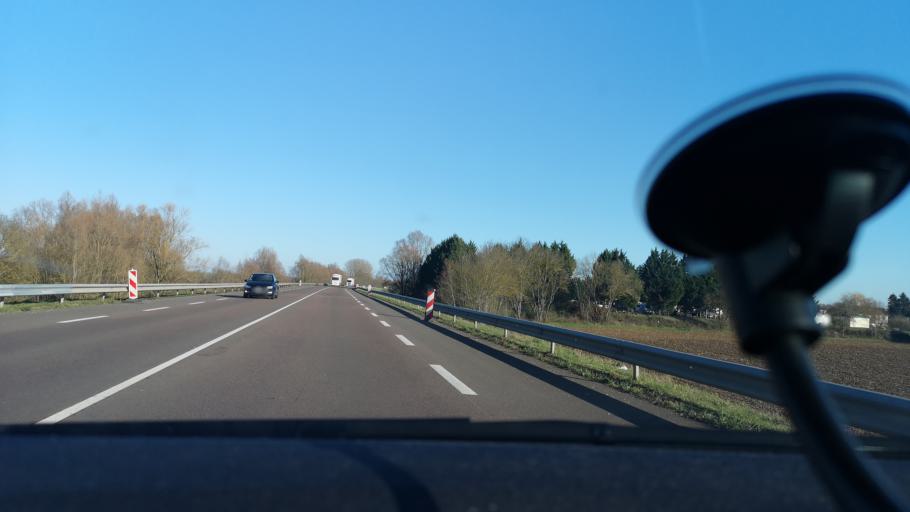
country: FR
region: Bourgogne
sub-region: Departement de Saone-et-Loire
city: Saint-Marcel
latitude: 46.7823
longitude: 4.8863
